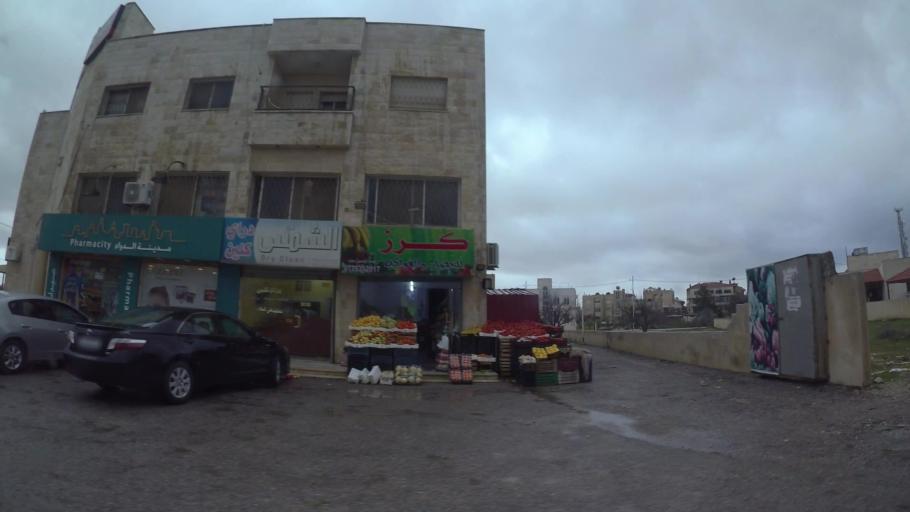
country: JO
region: Amman
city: Al Jubayhah
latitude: 32.0370
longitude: 35.8635
